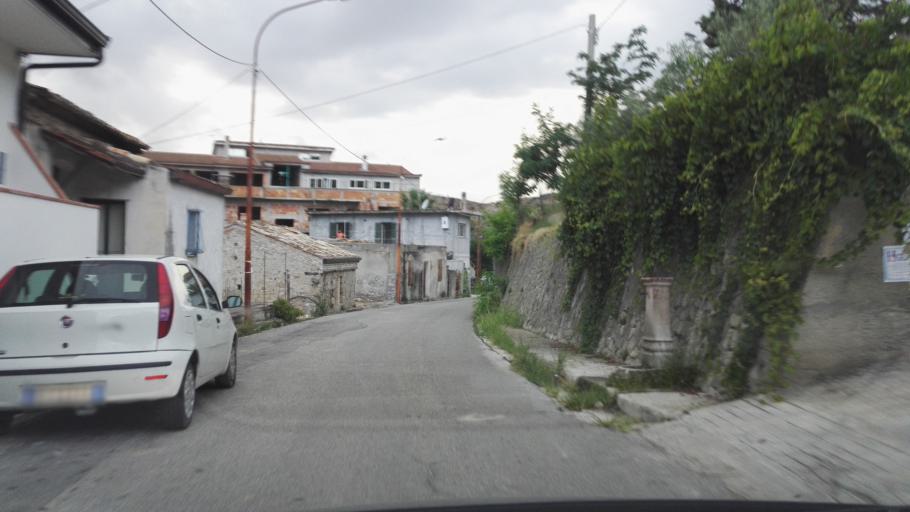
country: IT
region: Calabria
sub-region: Provincia di Reggio Calabria
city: Caulonia Marina
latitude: 38.3629
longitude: 16.4626
